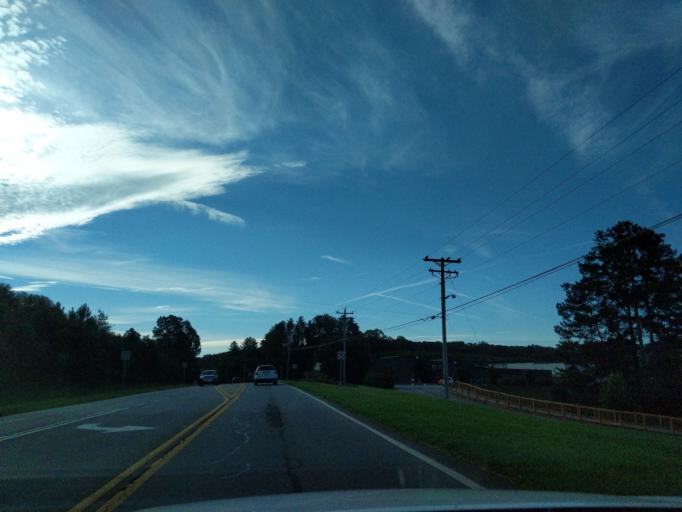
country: US
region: Georgia
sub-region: Fannin County
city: Blue Ridge
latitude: 34.8877
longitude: -84.3423
